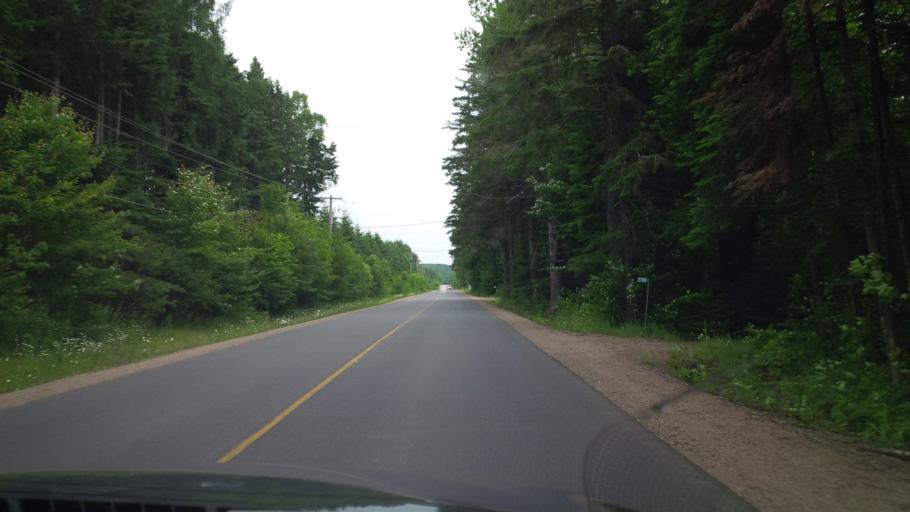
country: CA
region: Ontario
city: Huntsville
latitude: 45.5961
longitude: -79.2018
